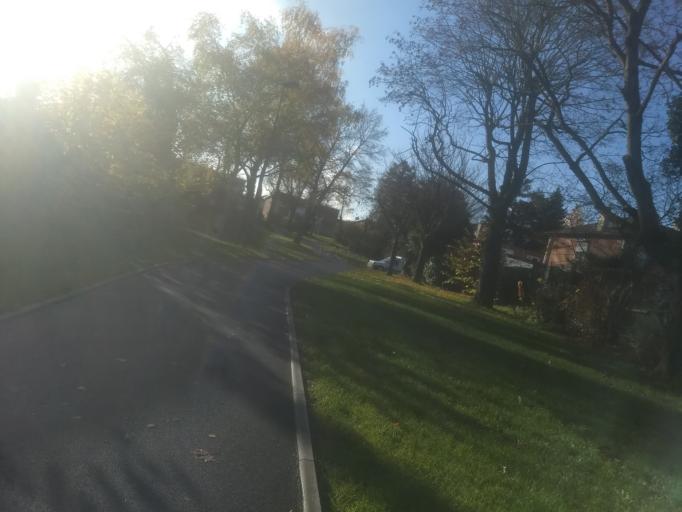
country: FR
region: Nord-Pas-de-Calais
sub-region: Departement du Pas-de-Calais
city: Anzin-Saint-Aubin
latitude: 50.2990
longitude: 2.7482
